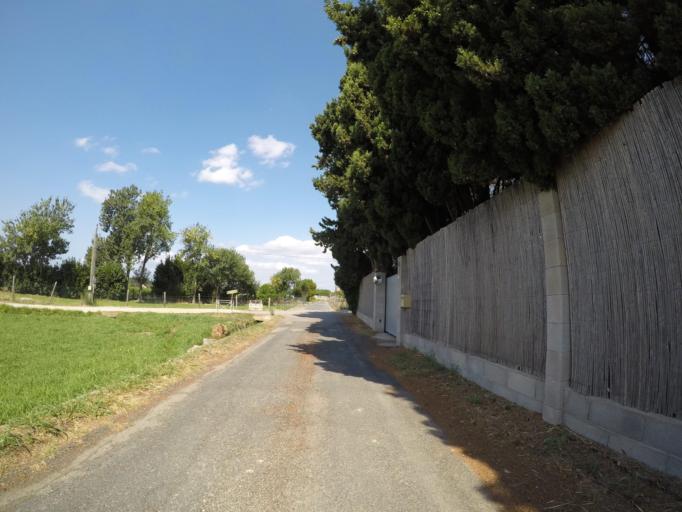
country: FR
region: Languedoc-Roussillon
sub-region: Departement des Pyrenees-Orientales
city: Saint-Esteve
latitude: 42.7019
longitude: 2.8623
